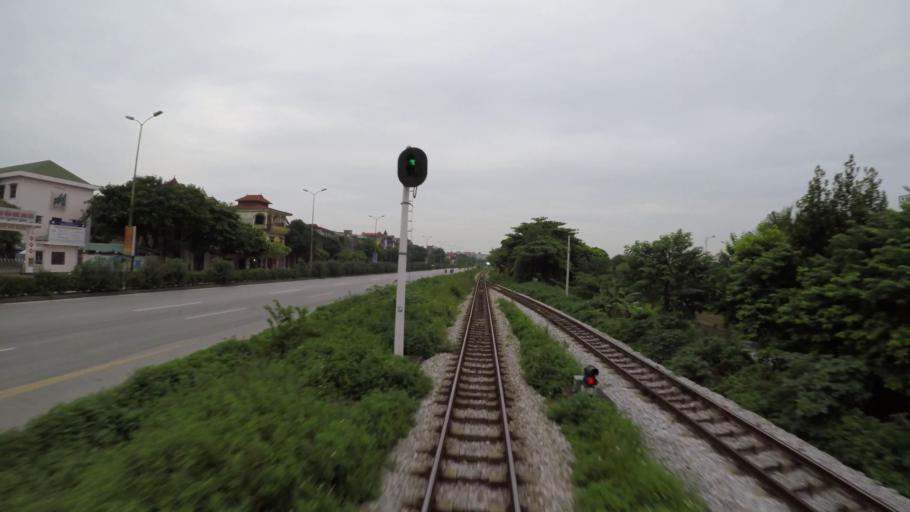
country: VN
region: Hung Yen
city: Nhu Quynh
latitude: 20.9988
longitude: 105.9688
